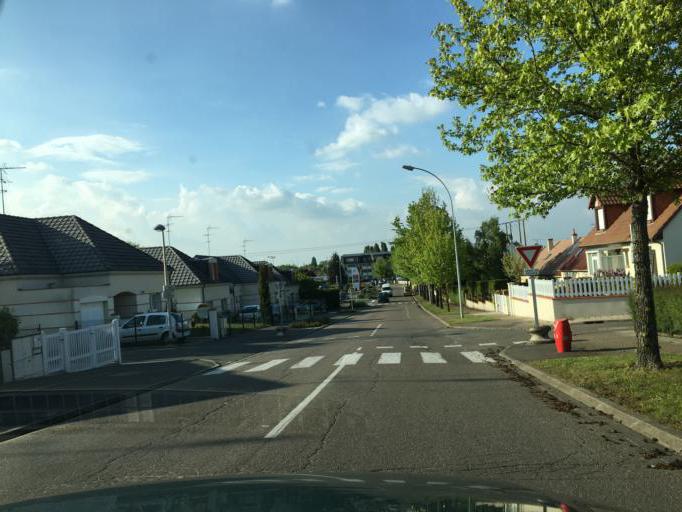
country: FR
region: Centre
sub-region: Departement du Loiret
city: Saran
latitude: 47.9348
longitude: 1.8896
